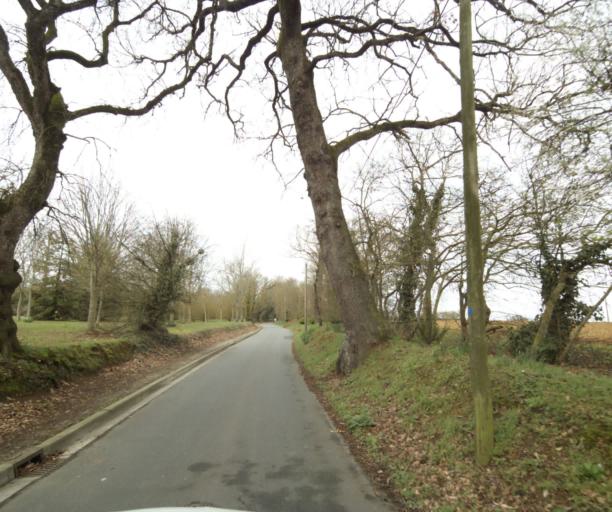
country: FR
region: Poitou-Charentes
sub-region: Departement de la Charente-Maritime
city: Lagord
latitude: 46.1887
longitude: -1.1633
